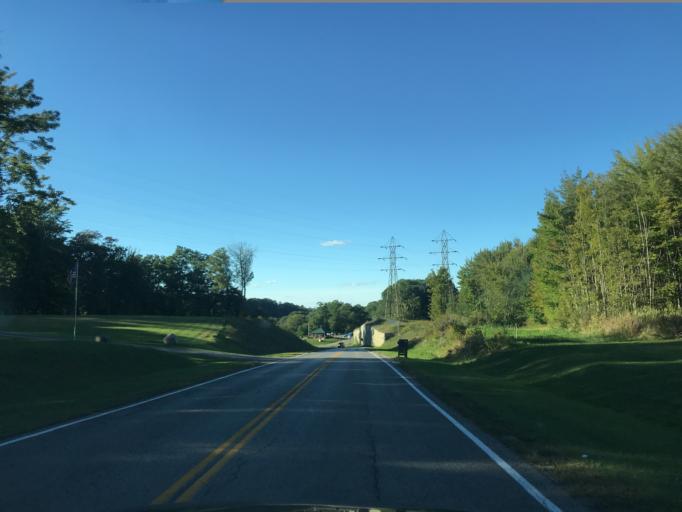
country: US
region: Ohio
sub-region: Ashtabula County
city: Edgewood
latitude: 41.8539
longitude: -80.7577
